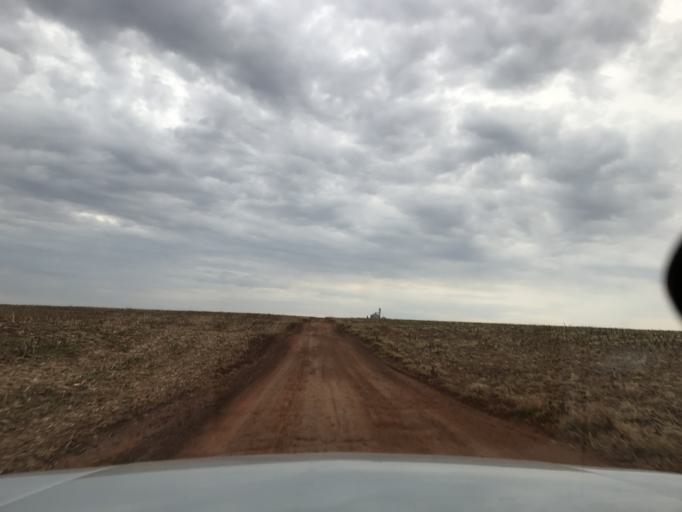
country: BR
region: Parana
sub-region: Palotina
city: Palotina
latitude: -24.2216
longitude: -53.8360
